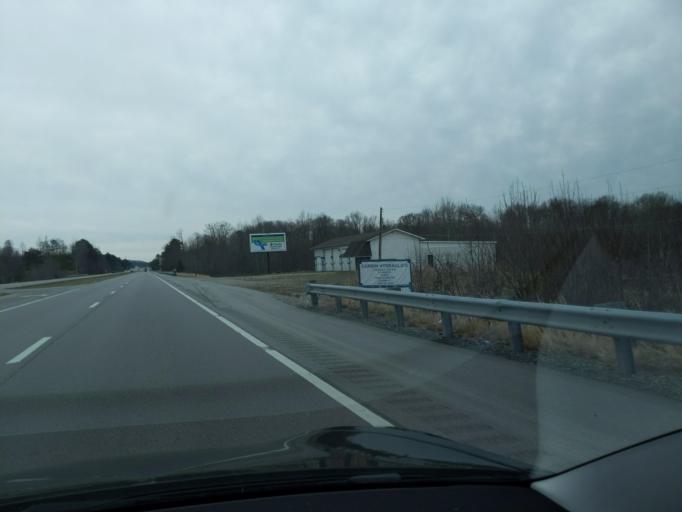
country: US
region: Kentucky
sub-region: Laurel County
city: North Corbin
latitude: 36.9447
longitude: -84.0185
